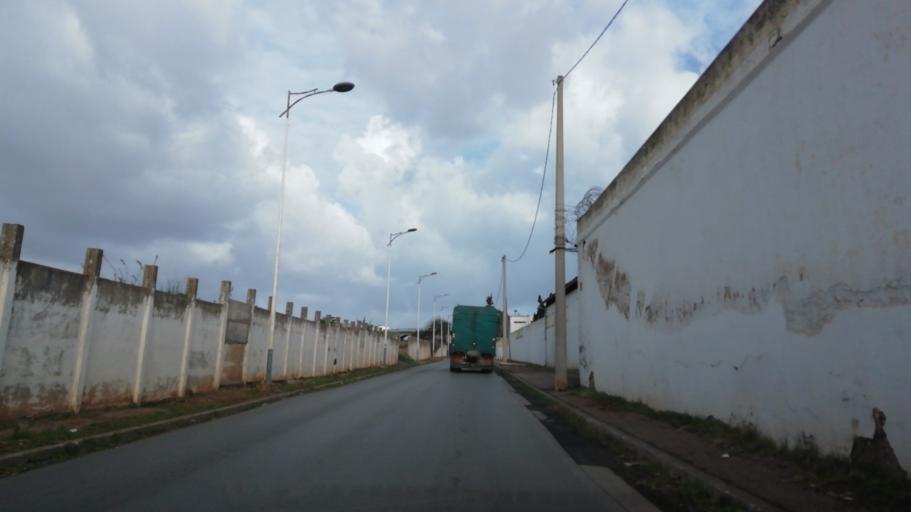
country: DZ
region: Oran
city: Oran
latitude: 35.6861
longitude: -0.6293
